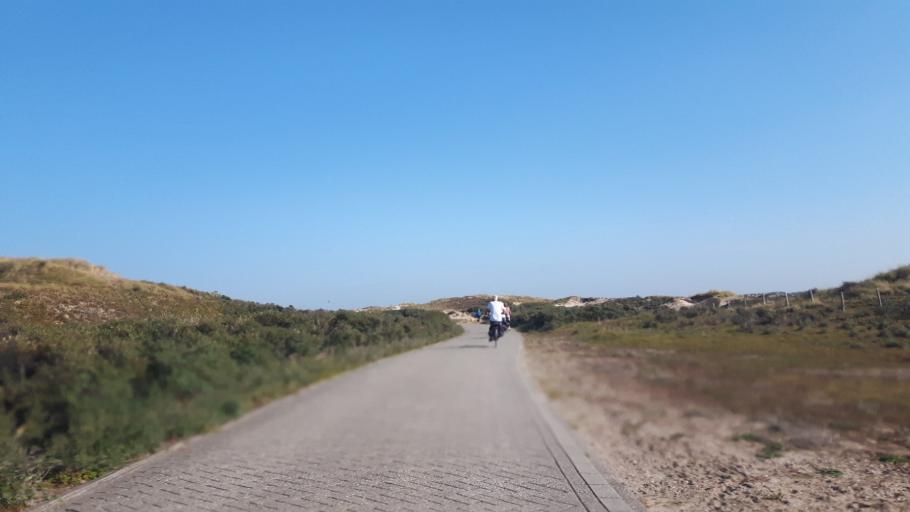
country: NL
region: South Holland
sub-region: Gemeente Noordwijkerhout
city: Noordwijkerhout
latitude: 52.2993
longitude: 4.4762
